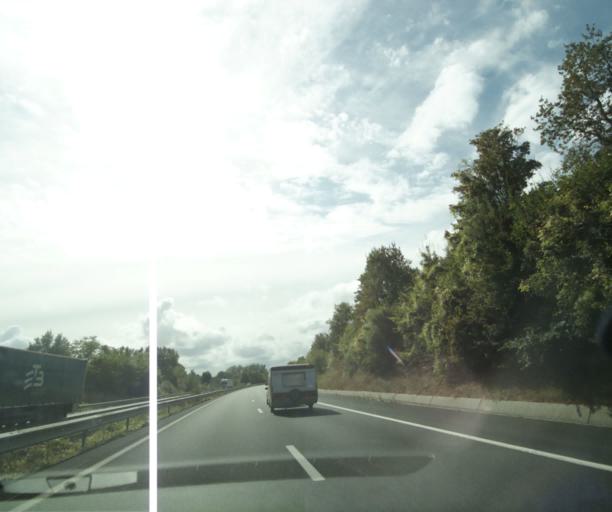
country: FR
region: Poitou-Charentes
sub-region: Departement de la Charente-Maritime
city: Pons
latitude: 45.6021
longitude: -0.5909
